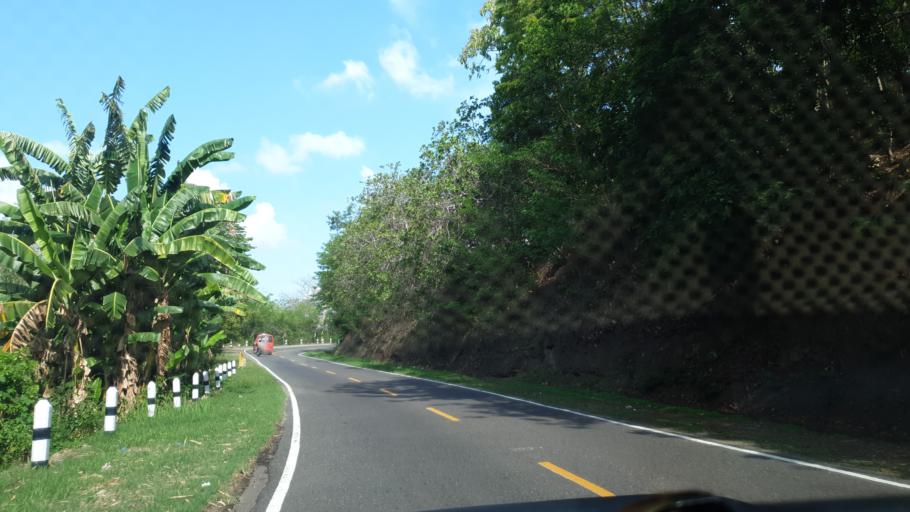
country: ID
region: East Nusa Tenggara
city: Nangalimang
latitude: -8.6611
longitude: 122.1985
